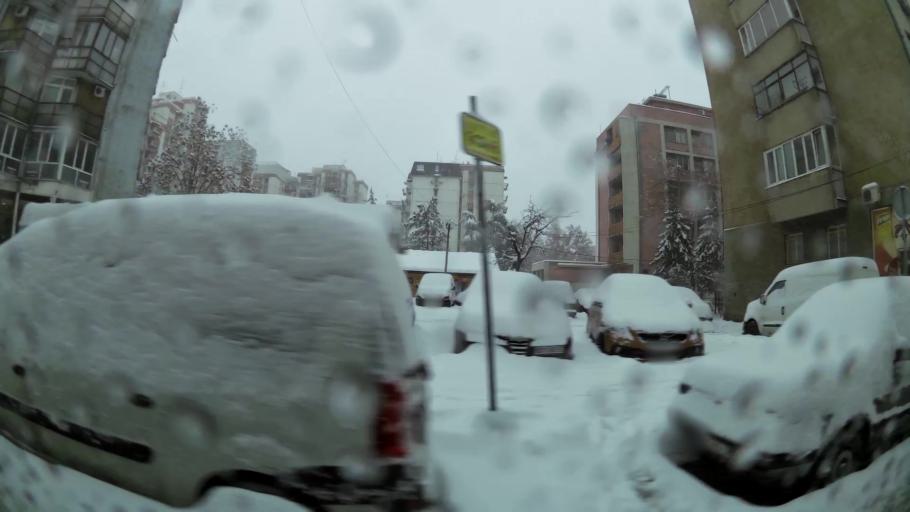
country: RS
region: Central Serbia
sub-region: Belgrade
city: Stari Grad
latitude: 44.8254
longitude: 20.4616
